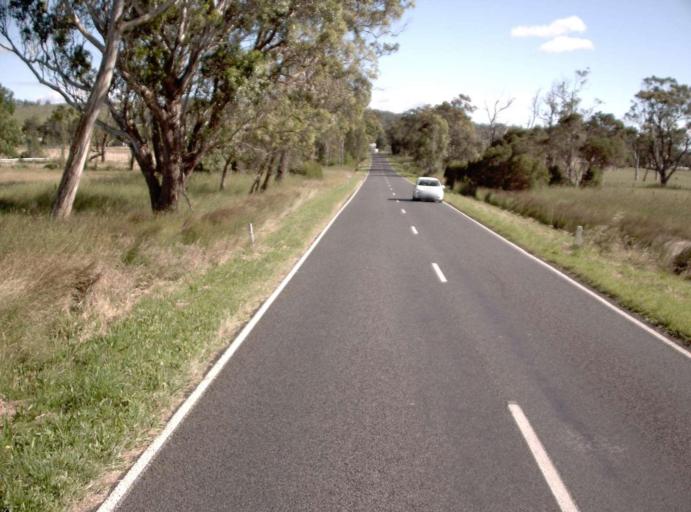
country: AU
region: Victoria
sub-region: Latrobe
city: Traralgon
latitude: -38.1561
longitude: 146.4927
